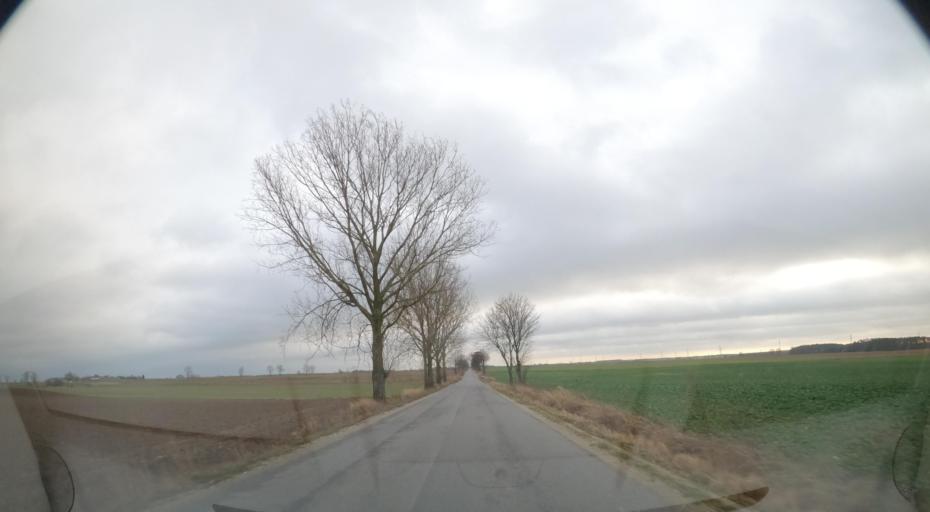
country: PL
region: Kujawsko-Pomorskie
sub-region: Powiat nakielski
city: Sadki
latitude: 53.2060
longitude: 17.3698
